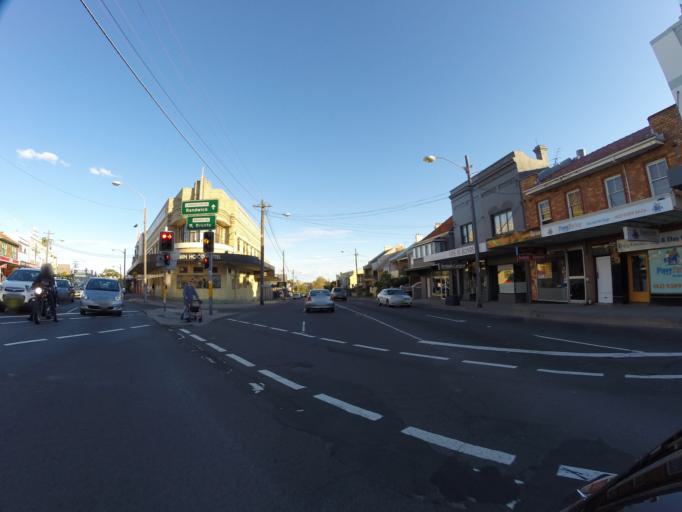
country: AU
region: New South Wales
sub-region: Waverley
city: Bondi Junction
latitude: -33.9004
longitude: 151.2536
